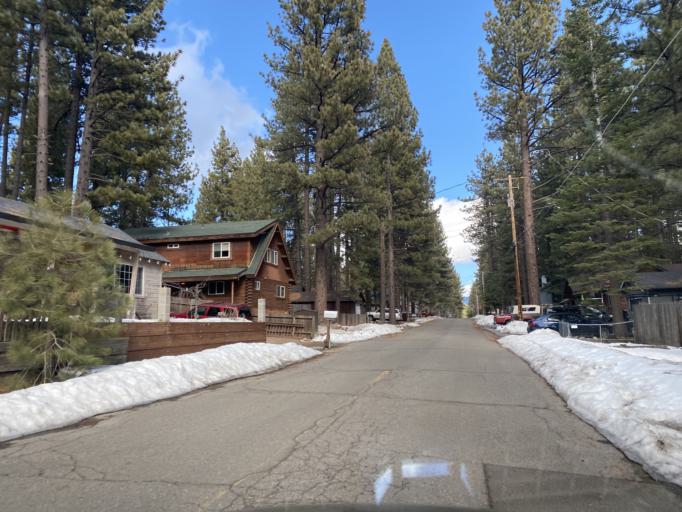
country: US
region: California
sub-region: El Dorado County
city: South Lake Tahoe
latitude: 38.9200
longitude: -119.9826
